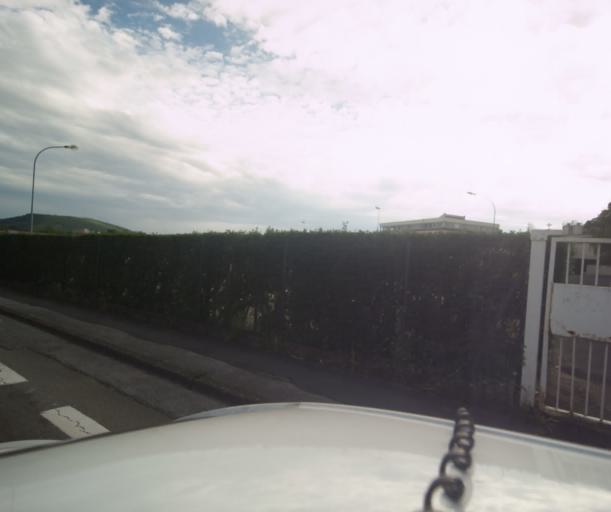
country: FR
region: Franche-Comte
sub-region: Departement du Doubs
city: Pirey
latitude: 47.2419
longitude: 5.9860
